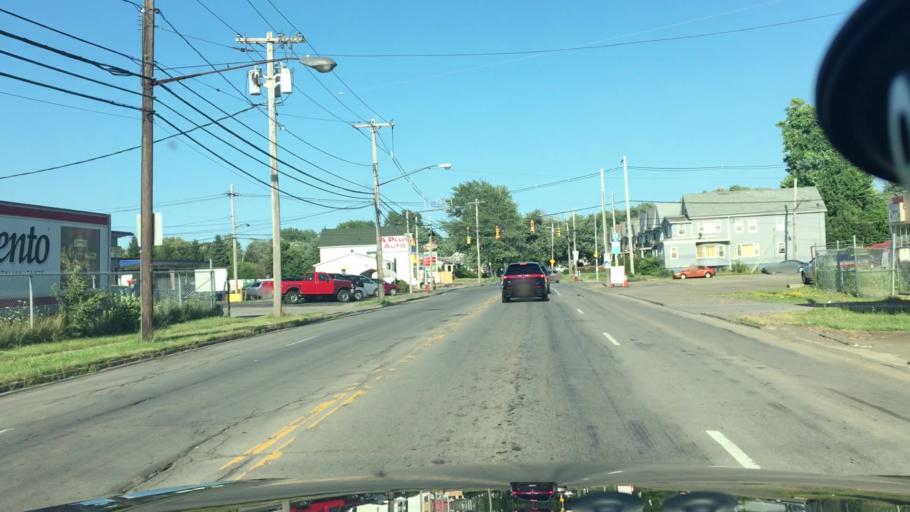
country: US
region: New York
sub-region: Erie County
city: Lackawanna
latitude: 42.8470
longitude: -78.8335
